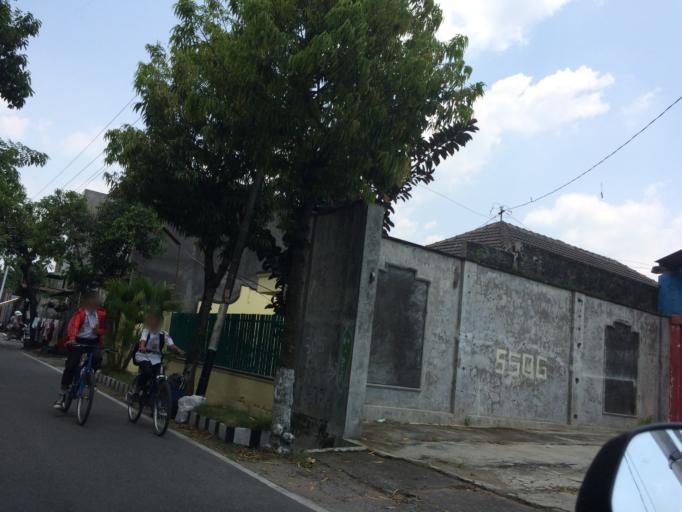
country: ID
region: Central Java
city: Grogol
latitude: -7.5929
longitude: 110.8205
